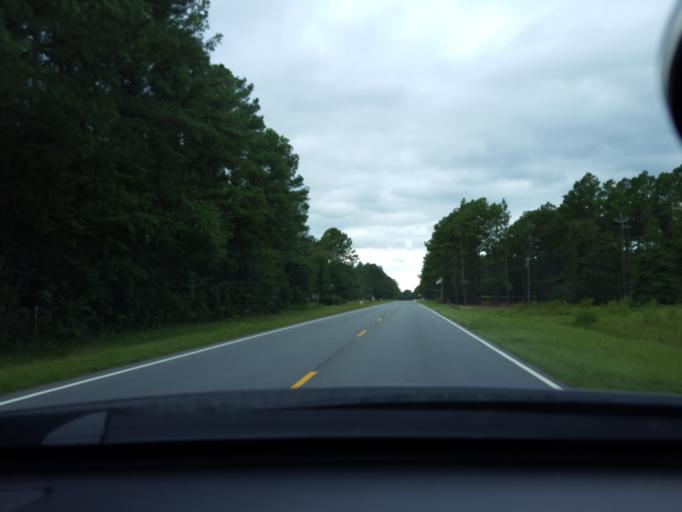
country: US
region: North Carolina
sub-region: Bladen County
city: Elizabethtown
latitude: 34.7100
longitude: -78.4592
